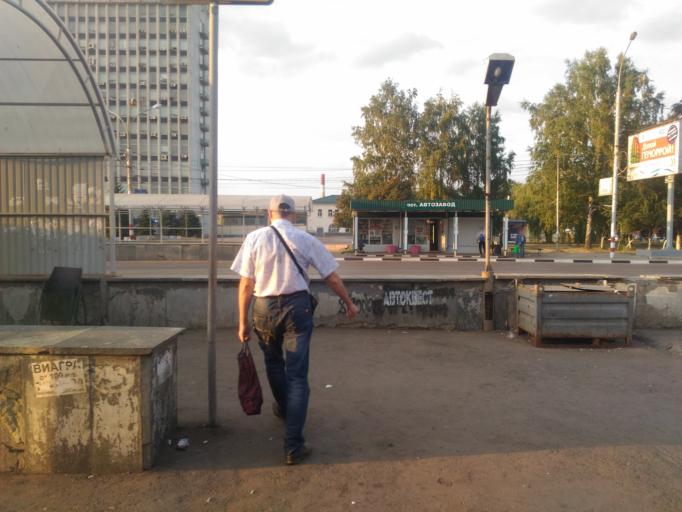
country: RU
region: Ulyanovsk
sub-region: Ulyanovskiy Rayon
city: Ulyanovsk
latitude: 54.3082
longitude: 48.3326
